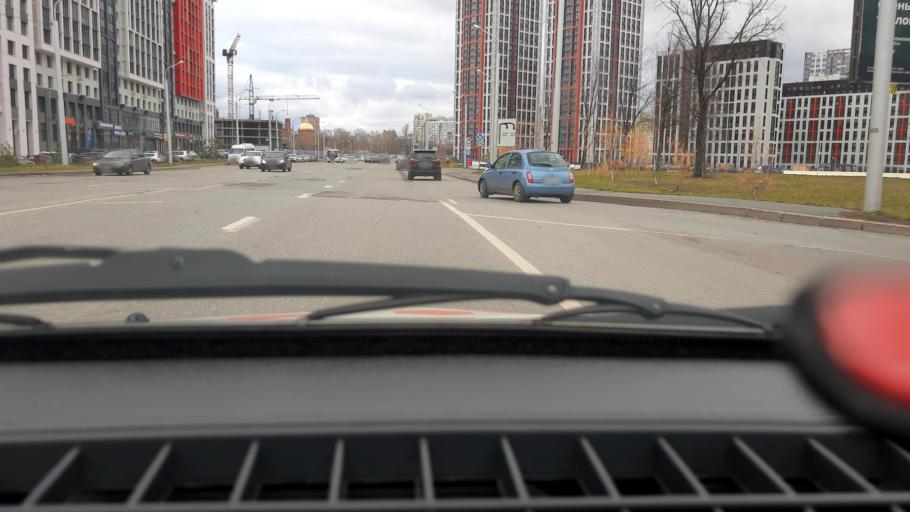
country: RU
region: Bashkortostan
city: Ufa
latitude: 54.7553
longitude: 56.0319
